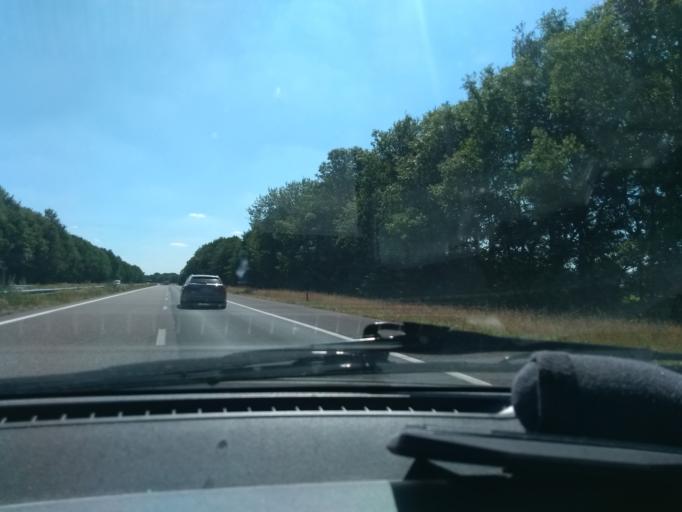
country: NL
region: Drenthe
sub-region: Gemeente Emmen
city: Klazienaveen
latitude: 52.7265
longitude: 7.0499
